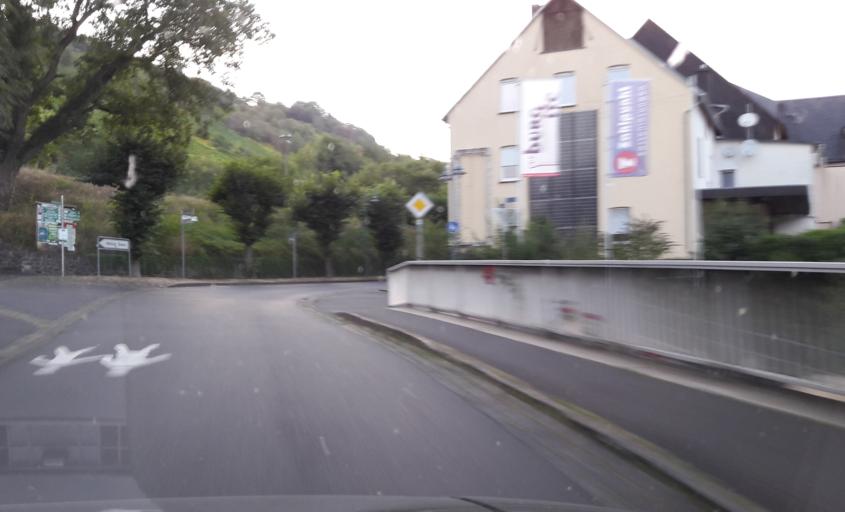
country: DE
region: Rheinland-Pfalz
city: Reil
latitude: 50.0237
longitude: 7.1143
